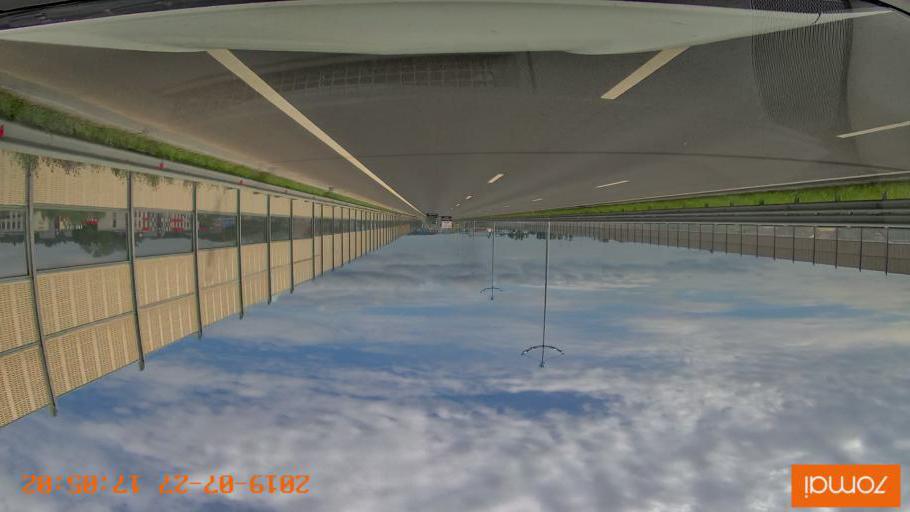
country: RU
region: Kaliningrad
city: Bol'shoe Isakovo
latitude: 54.7238
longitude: 20.5975
